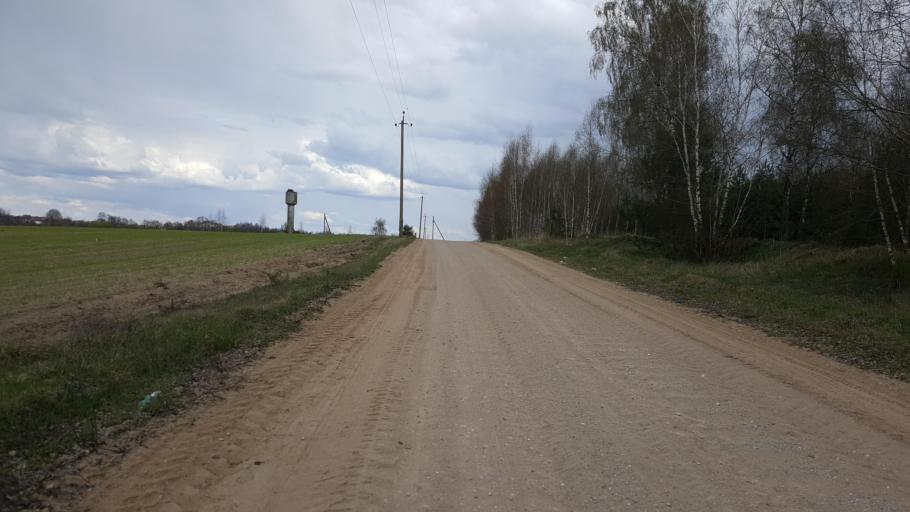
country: BY
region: Brest
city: Kamyanyets
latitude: 52.3956
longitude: 23.7472
